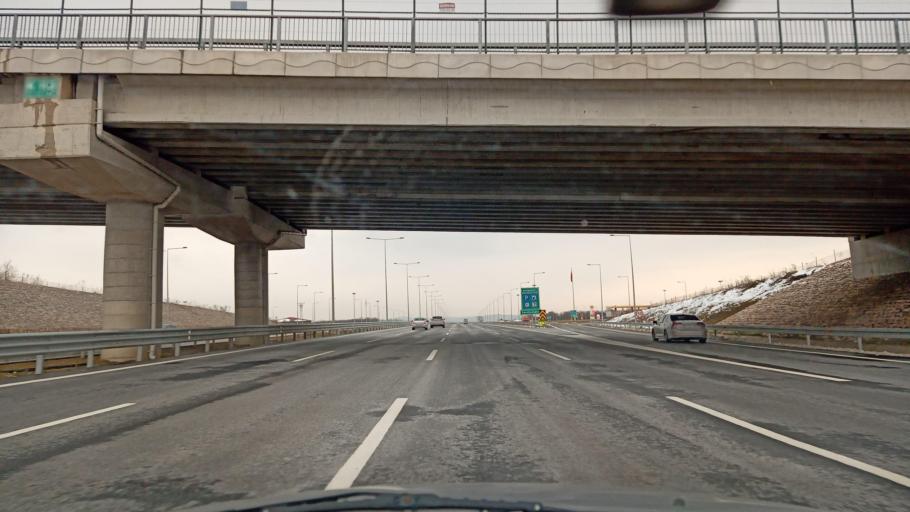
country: TR
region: Sakarya
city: Kazimpasa
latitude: 40.8445
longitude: 30.2795
